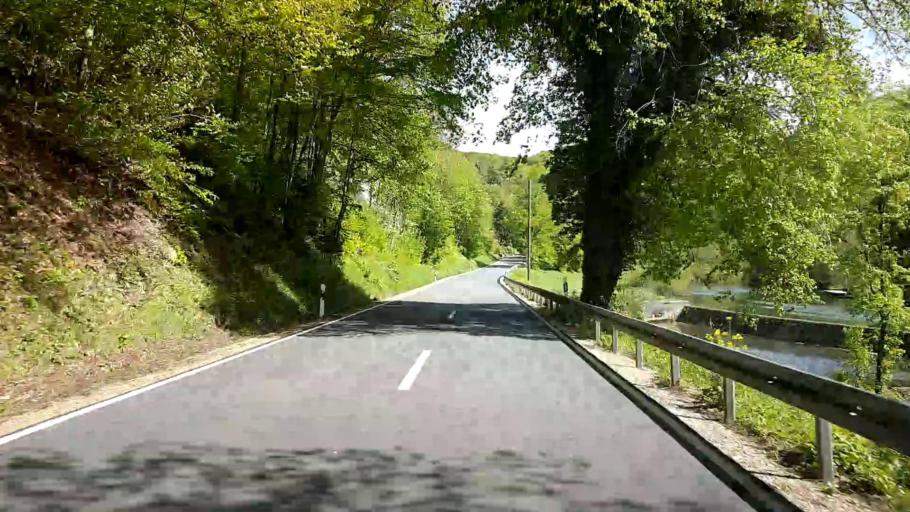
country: DE
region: Bavaria
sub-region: Upper Franconia
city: Gossweinstein
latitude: 49.7745
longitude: 11.3102
